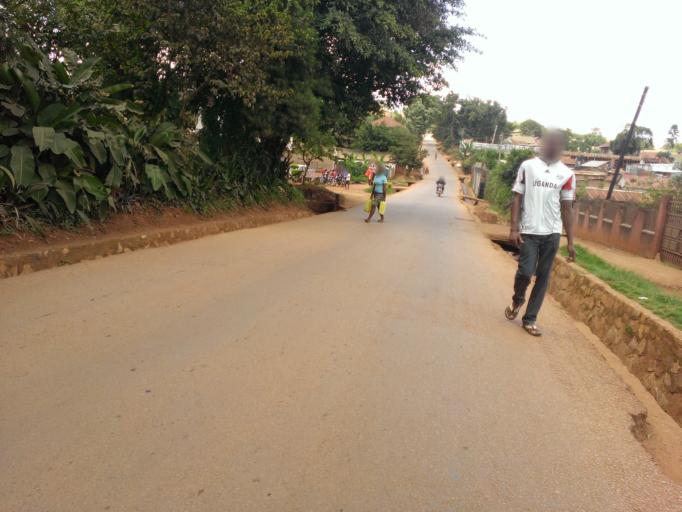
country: UG
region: Central Region
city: Kampala Central Division
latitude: 0.3229
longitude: 32.5538
